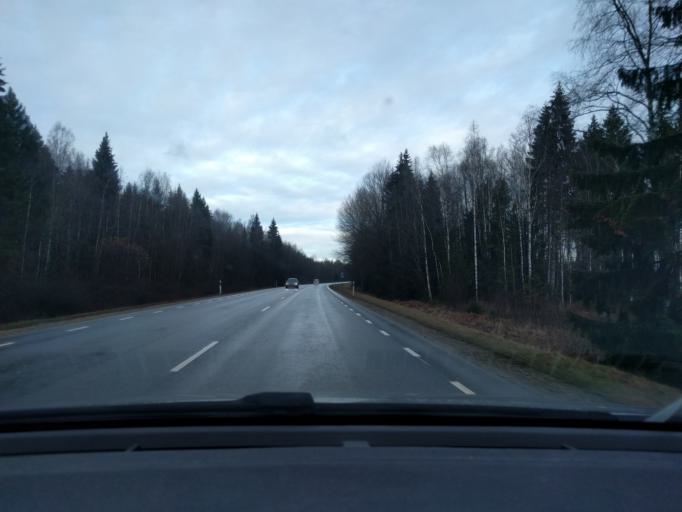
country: EE
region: Viljandimaa
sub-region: Vohma linn
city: Vohma
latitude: 58.5747
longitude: 25.5698
